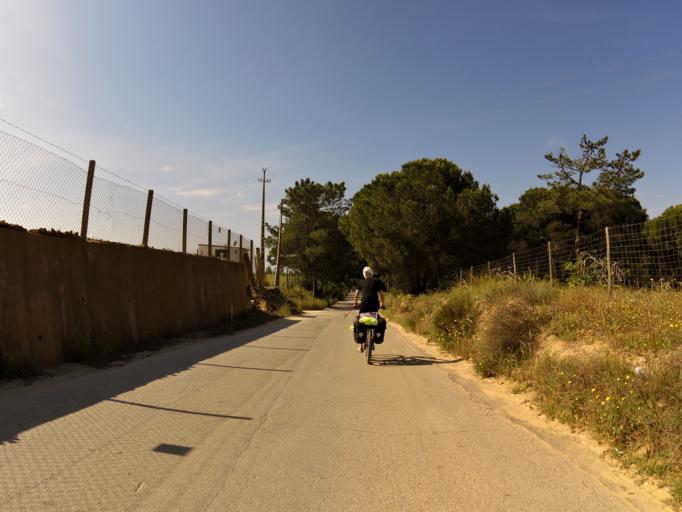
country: PT
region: Faro
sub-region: Loule
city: Almancil
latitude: 37.0654
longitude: -8.0149
